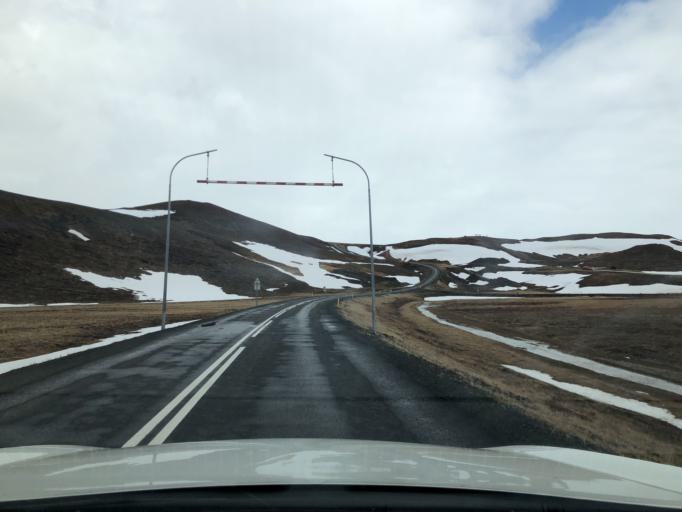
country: IS
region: Northeast
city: Laugar
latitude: 65.7046
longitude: -16.7717
